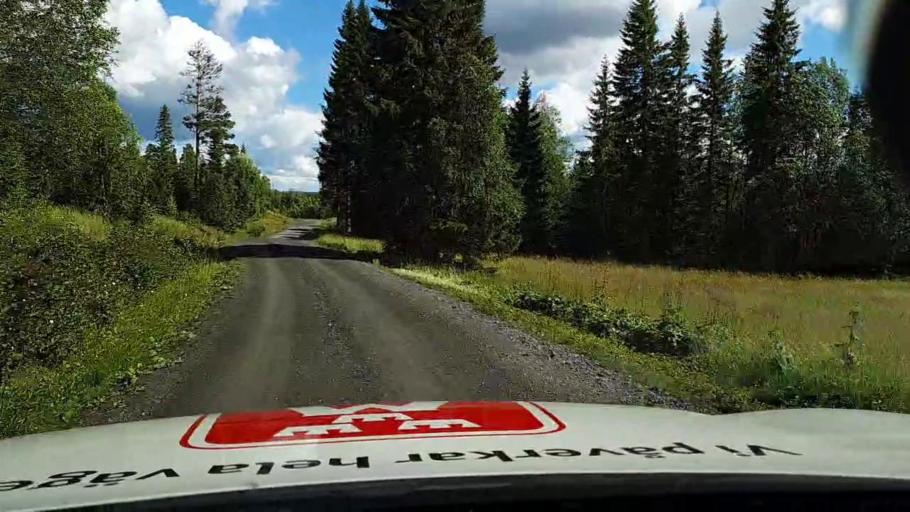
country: SE
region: Jaemtland
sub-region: Krokoms Kommun
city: Valla
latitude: 63.3277
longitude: 13.7354
